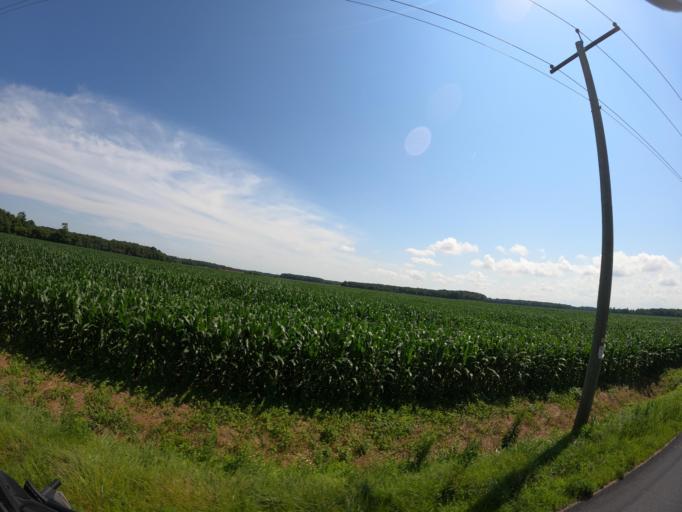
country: US
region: Maryland
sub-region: Worcester County
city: Ocean Pines
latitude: 38.4514
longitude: -75.1596
